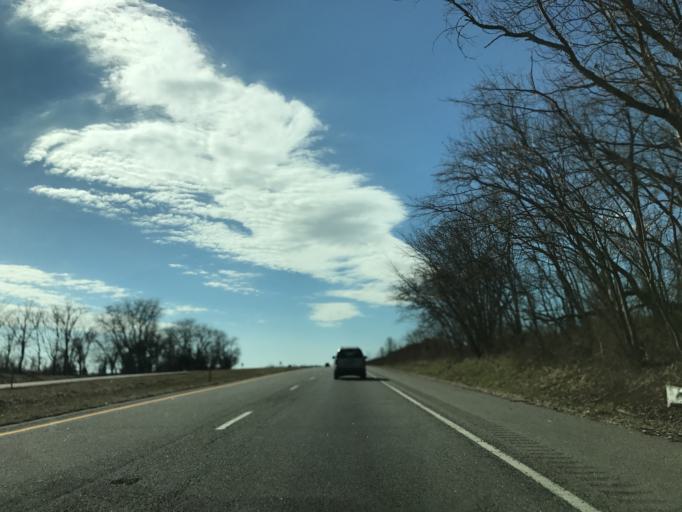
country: US
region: Delaware
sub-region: New Castle County
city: Middletown
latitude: 39.3757
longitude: -75.8100
